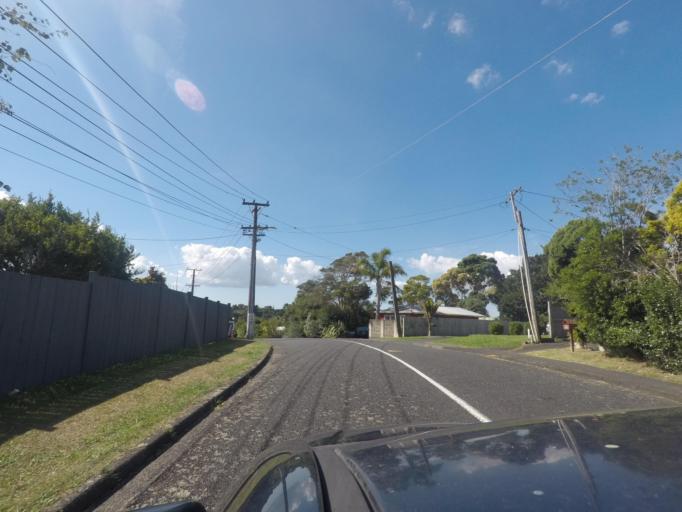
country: NZ
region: Auckland
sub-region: Auckland
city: Waitakere
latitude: -36.9268
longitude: 174.6586
